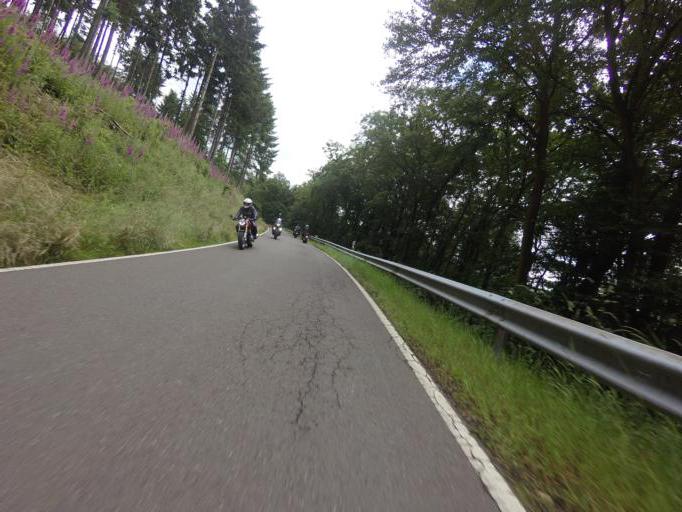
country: DE
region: Rheinland-Pfalz
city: Karbach
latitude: 50.1420
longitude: 7.6177
